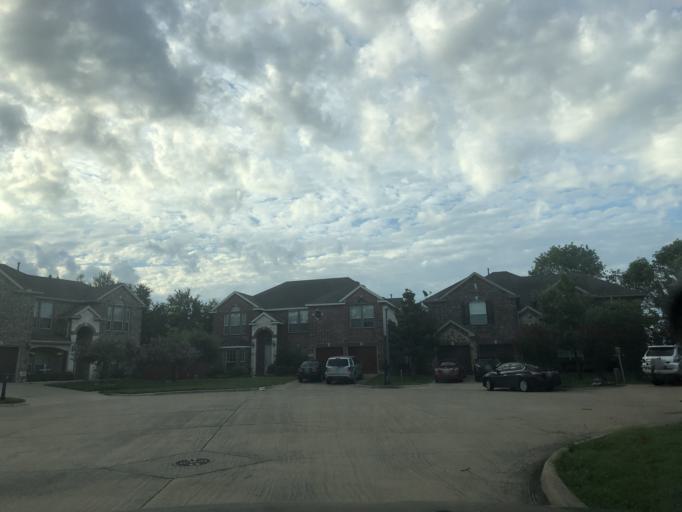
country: US
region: Texas
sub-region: Dallas County
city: Sunnyvale
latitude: 32.8483
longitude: -96.5875
